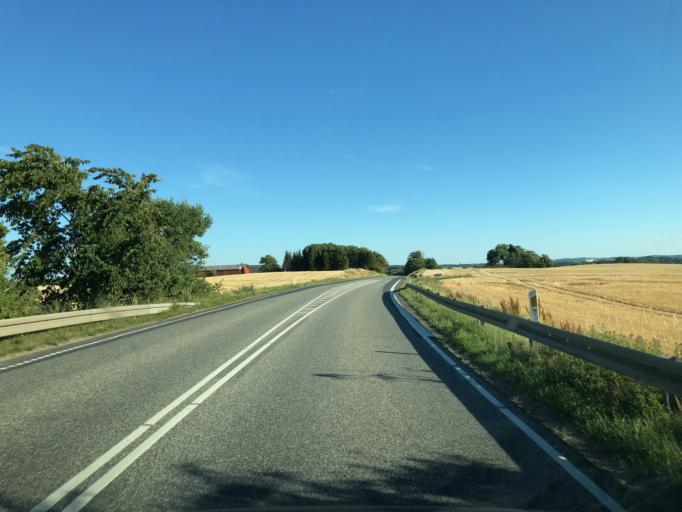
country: DK
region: Central Jutland
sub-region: Skanderborg Kommune
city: Stilling
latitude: 56.0762
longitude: 9.9760
